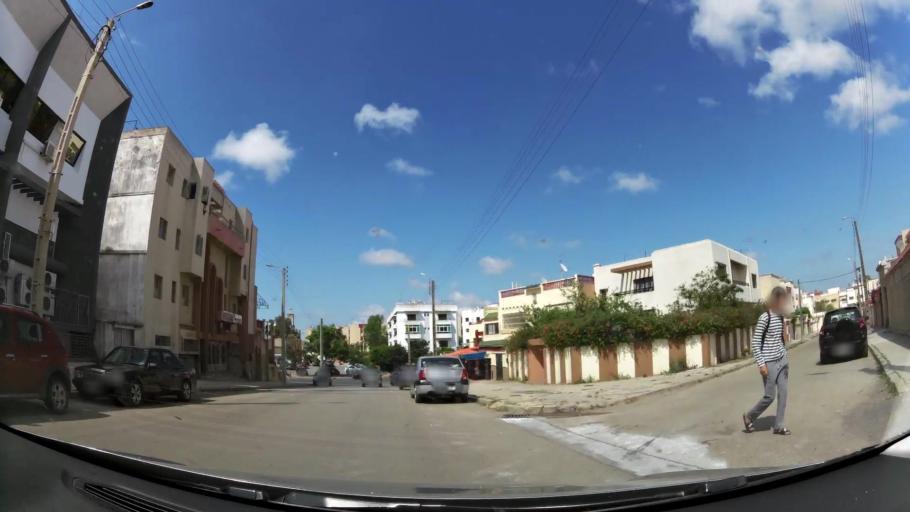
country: MA
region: Rabat-Sale-Zemmour-Zaer
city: Sale
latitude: 34.0398
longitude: -6.7889
